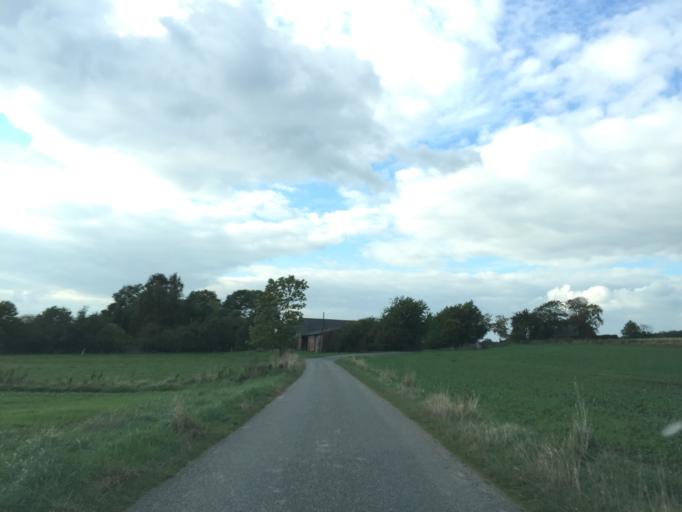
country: DK
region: Central Jutland
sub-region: Viborg Kommune
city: Bjerringbro
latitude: 56.2517
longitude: 9.6865
